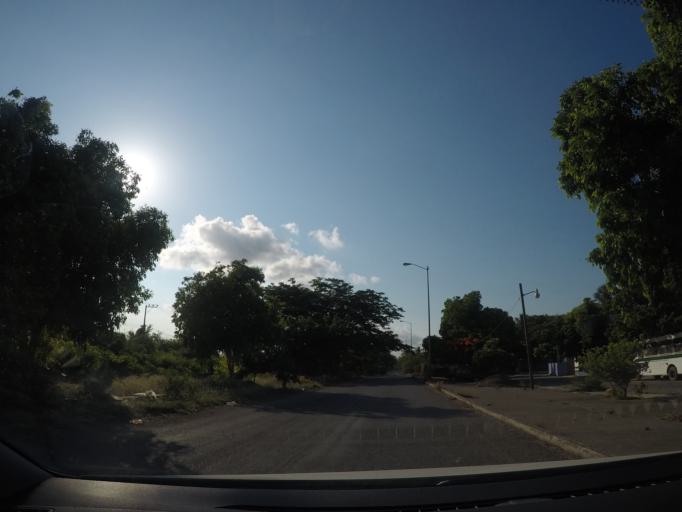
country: MX
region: Oaxaca
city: Juchitan de Zaragoza
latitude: 16.4241
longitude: -95.0297
